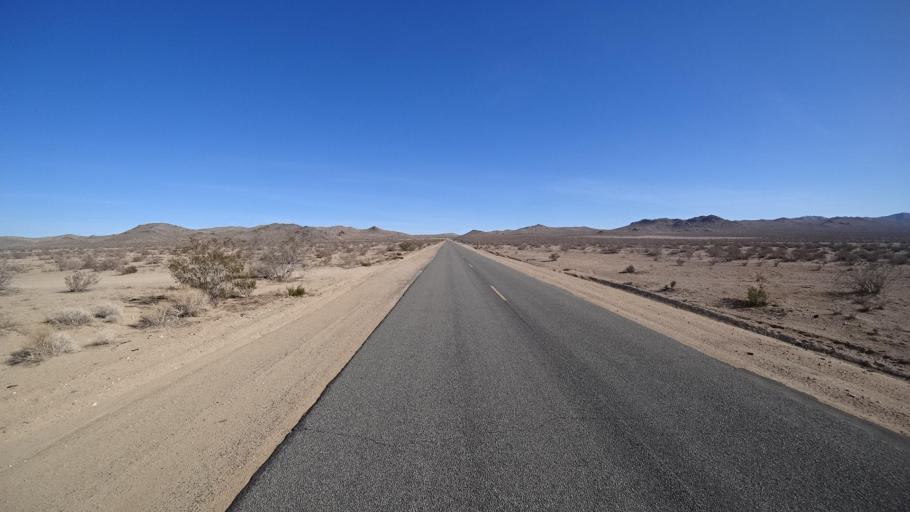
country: US
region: California
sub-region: Kern County
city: Ridgecrest
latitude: 35.5514
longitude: -117.7231
